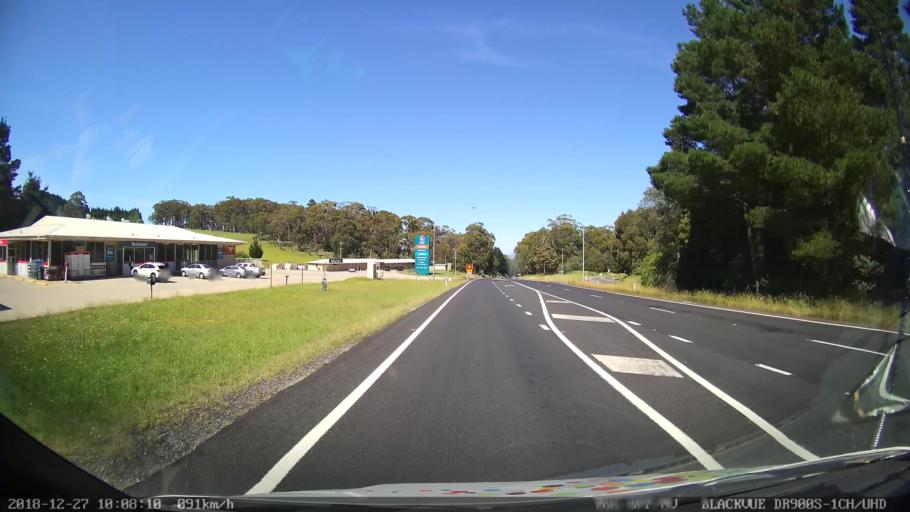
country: AU
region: New South Wales
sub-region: Lithgow
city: Portland
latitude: -33.4460
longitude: 149.8298
